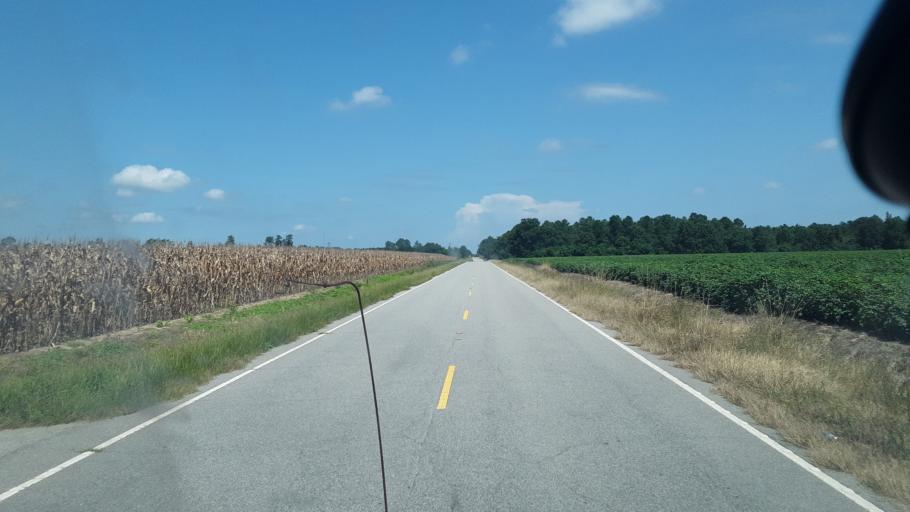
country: US
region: South Carolina
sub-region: Bamberg County
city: Bamberg
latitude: 33.3987
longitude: -81.0151
